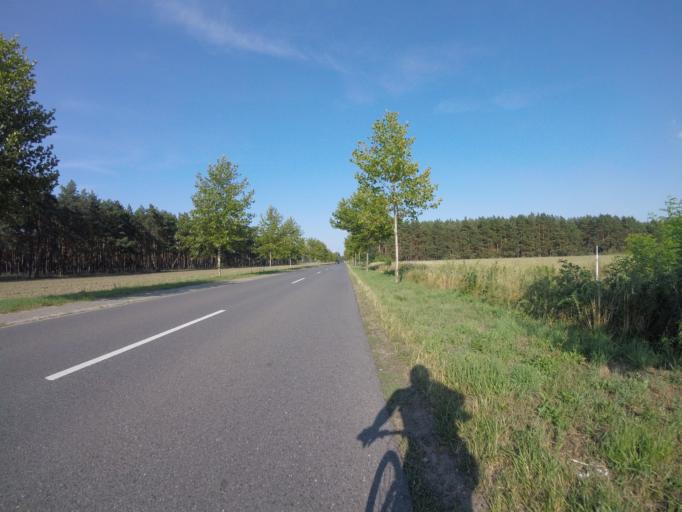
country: DE
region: Brandenburg
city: Bliesdorf
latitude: 52.6904
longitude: 14.1481
